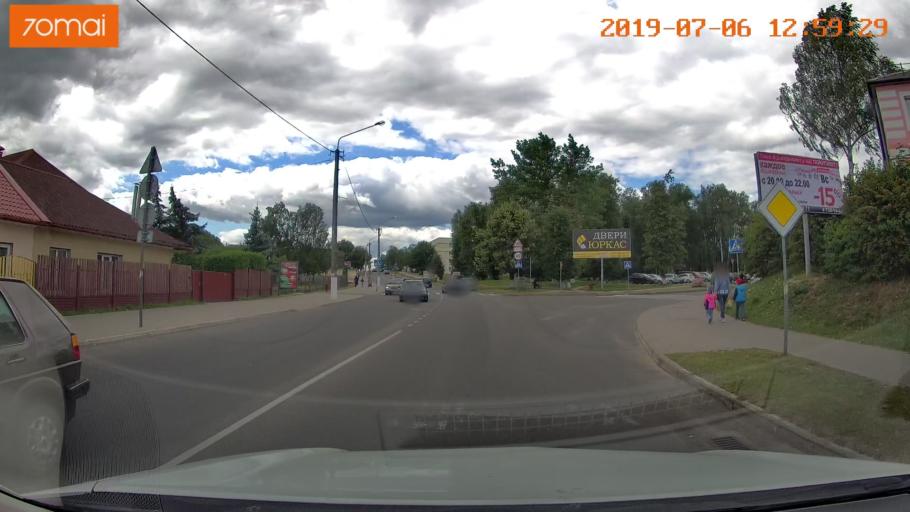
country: BY
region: Minsk
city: Dzyarzhynsk
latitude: 53.6862
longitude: 27.1358
